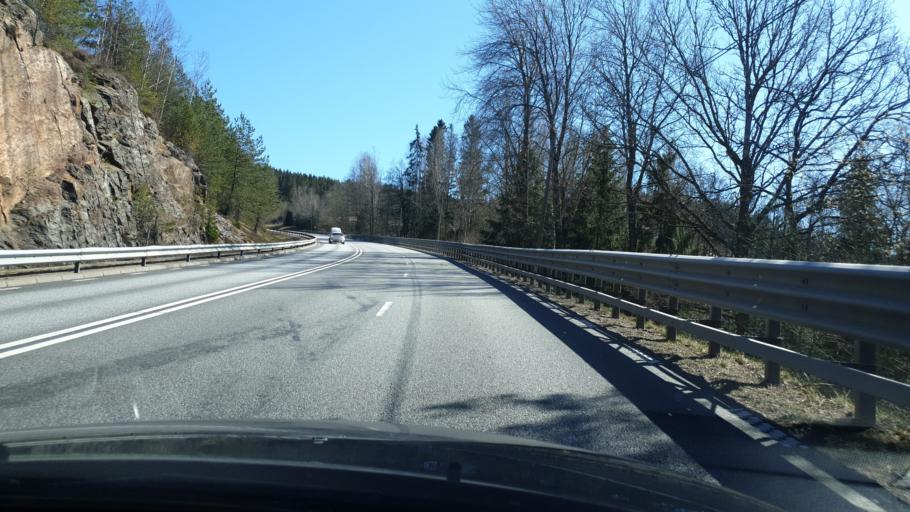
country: SE
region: Vaestra Goetaland
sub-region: Tanums Kommun
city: Tanumshede
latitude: 58.7944
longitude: 11.5740
